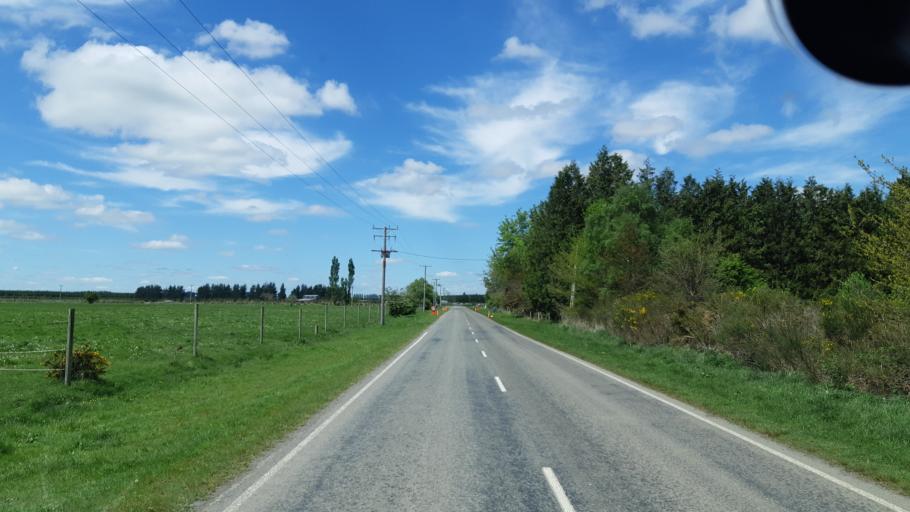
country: NZ
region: Canterbury
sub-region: Ashburton District
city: Methven
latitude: -43.6636
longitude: 171.4598
